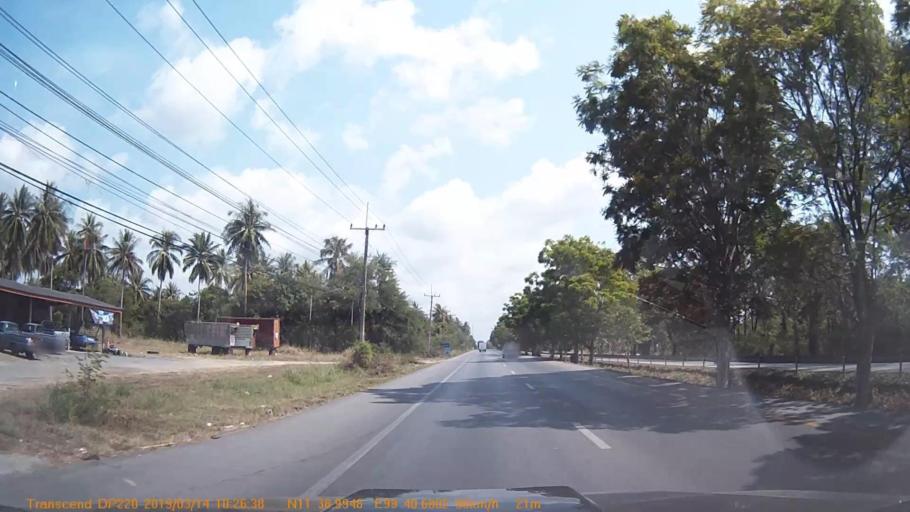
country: TH
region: Prachuap Khiri Khan
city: Thap Sakae
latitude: 11.6413
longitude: 99.6750
